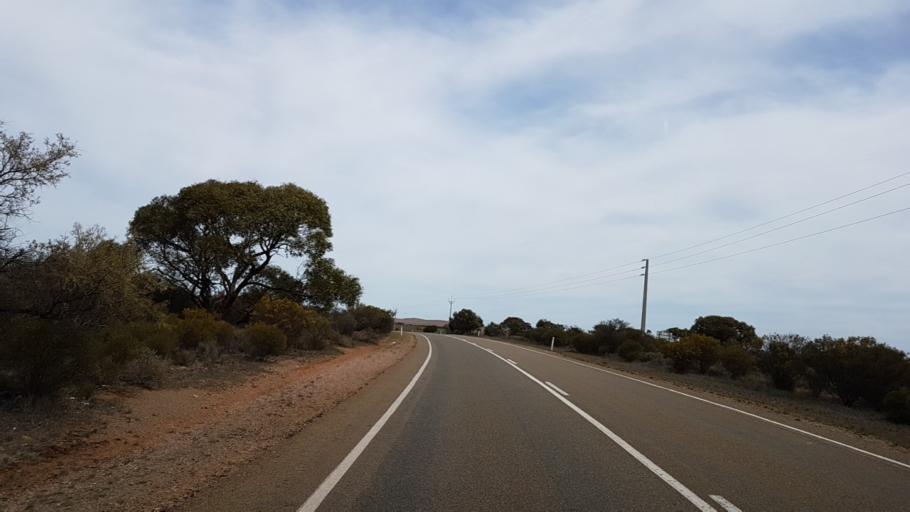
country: AU
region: South Australia
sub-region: Peterborough
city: Peterborough
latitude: -32.9909
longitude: 138.7906
